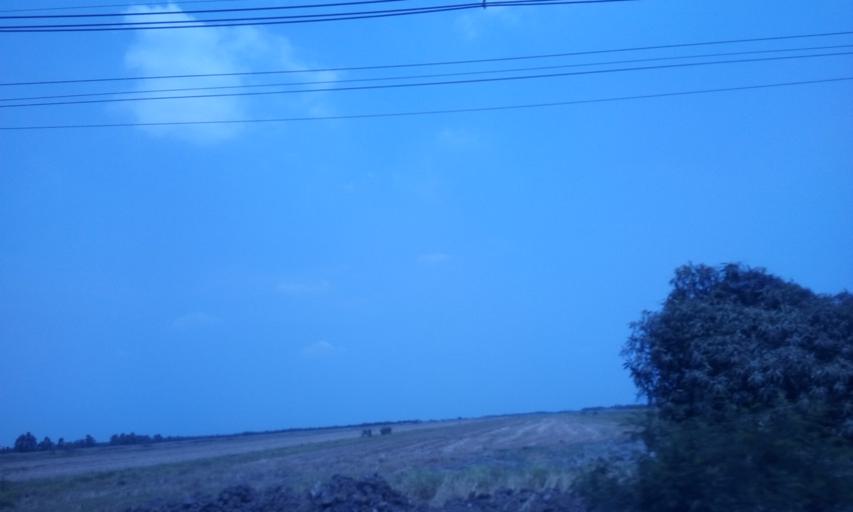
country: TH
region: Bangkok
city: Nong Chok
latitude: 13.9659
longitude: 100.9270
